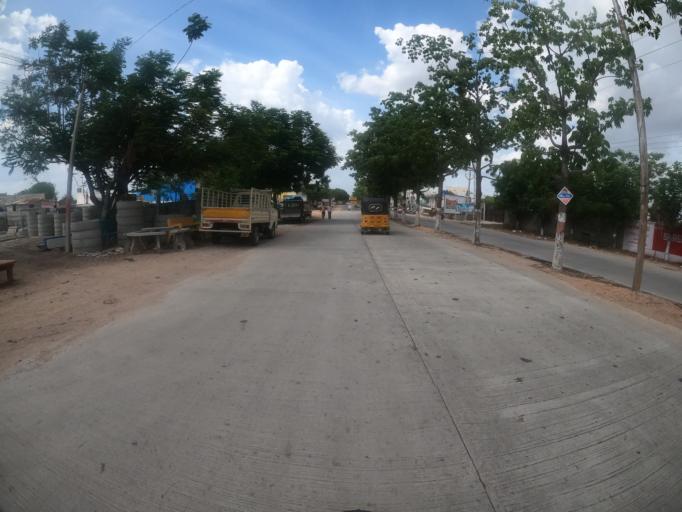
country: IN
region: Telangana
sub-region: Rangareddi
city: Sriramnagar
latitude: 17.3254
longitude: 78.2691
